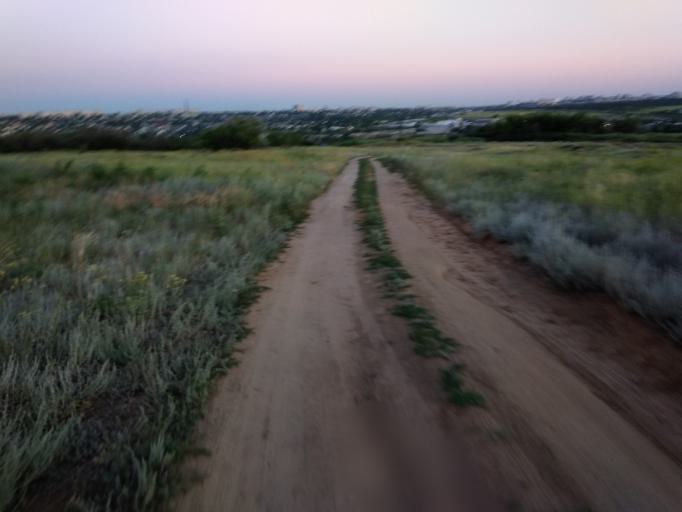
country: RU
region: Volgograd
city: Vodstroy
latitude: 48.8050
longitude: 44.5378
